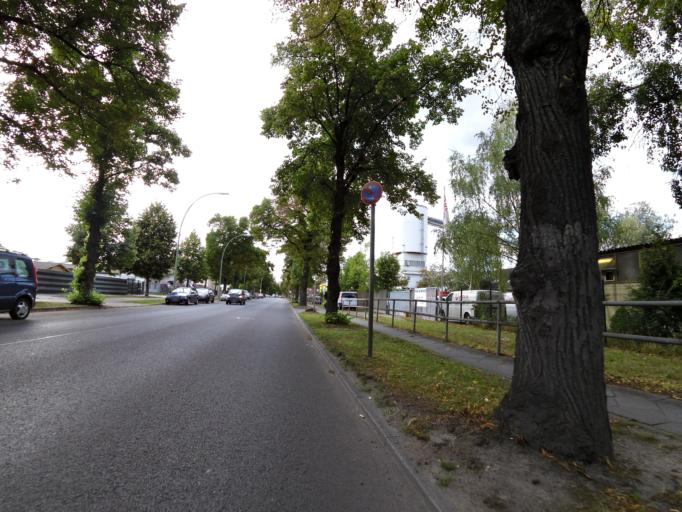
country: DE
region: Berlin
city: Johannisthal
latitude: 52.4275
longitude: 13.5047
